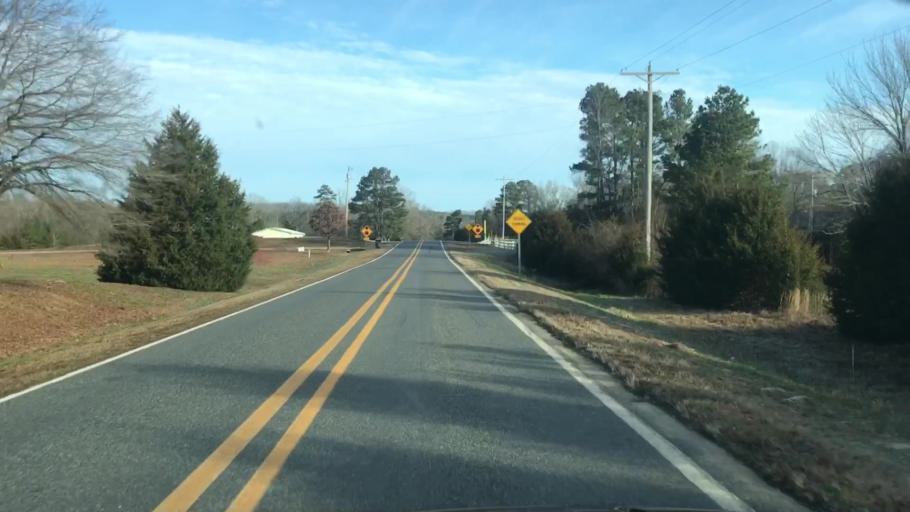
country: US
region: Arkansas
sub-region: Garland County
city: Rockwell
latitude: 34.5062
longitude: -93.2762
